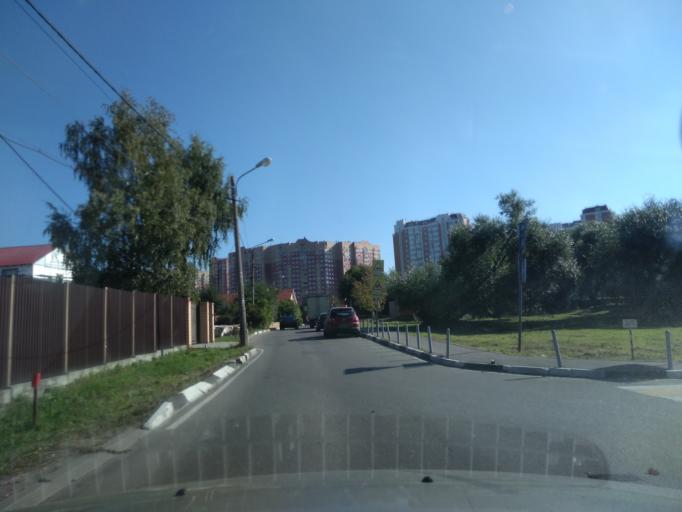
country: RU
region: Moscow
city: Strogino
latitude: 55.8609
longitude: 37.3866
